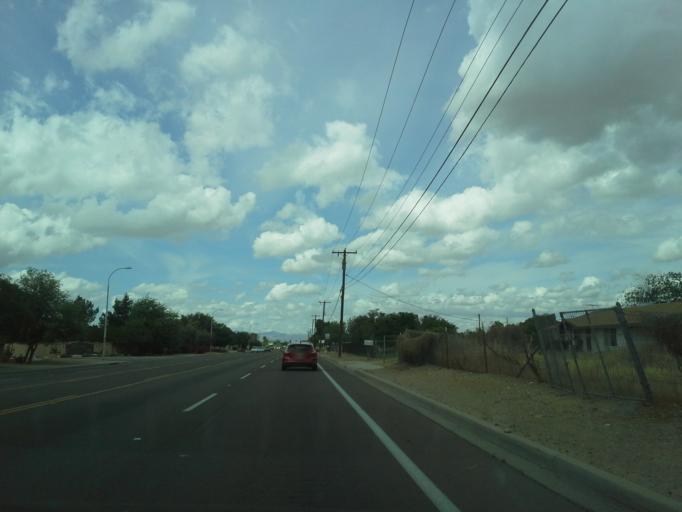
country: US
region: Arizona
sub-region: Maricopa County
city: Peoria
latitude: 33.6105
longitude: -112.2131
